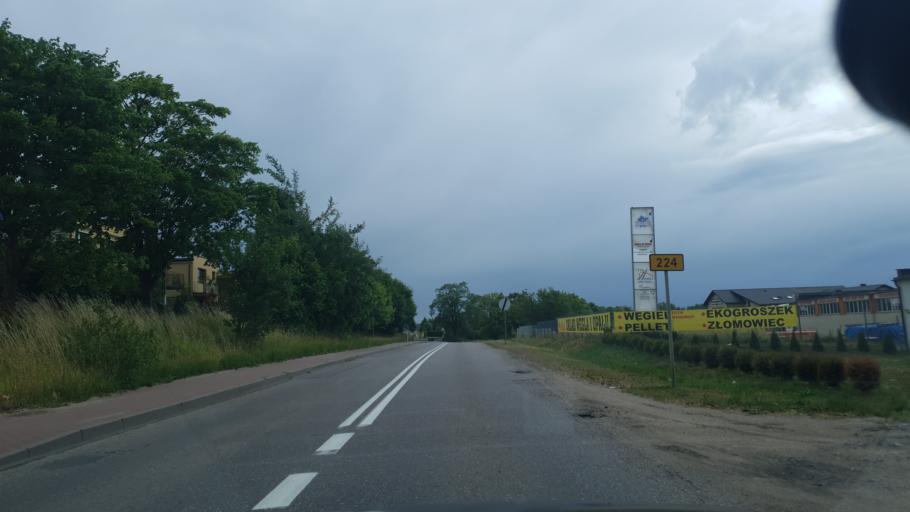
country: PL
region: Pomeranian Voivodeship
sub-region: Powiat kartuski
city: Przodkowo
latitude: 54.3748
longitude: 18.2831
